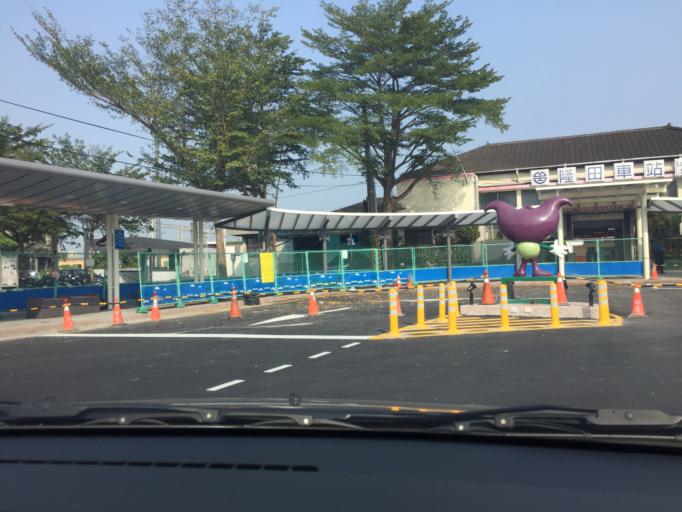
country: TW
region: Taiwan
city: Xinying
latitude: 23.1927
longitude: 120.3189
